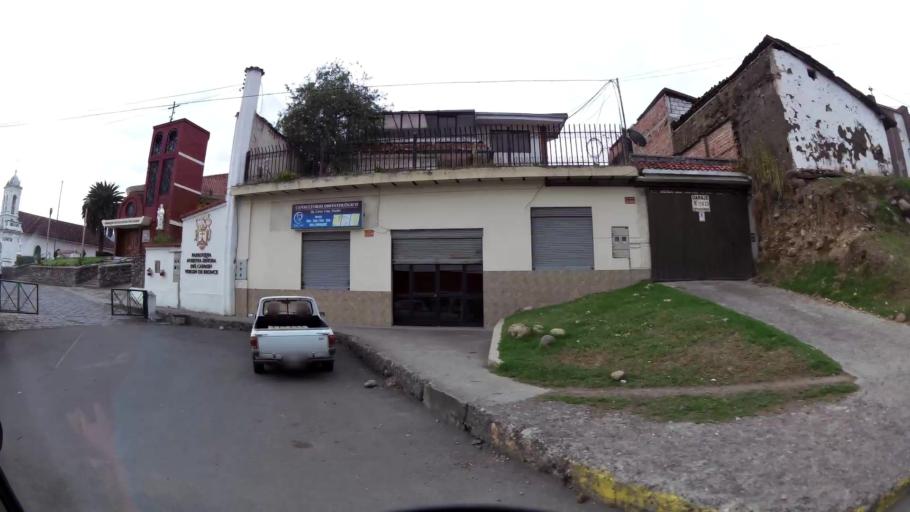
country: EC
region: Azuay
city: Cuenca
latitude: -2.9107
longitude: -79.0097
